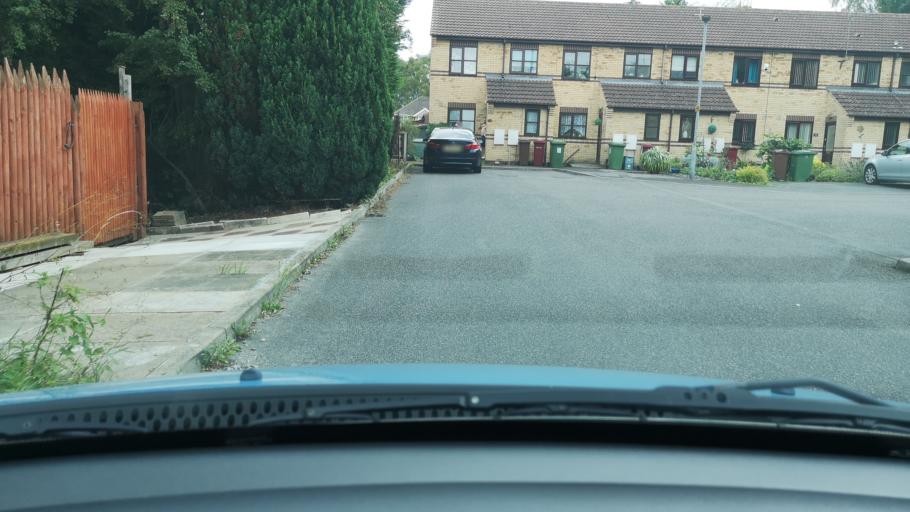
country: GB
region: England
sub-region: North Lincolnshire
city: Scunthorpe
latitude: 53.5855
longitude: -0.6855
